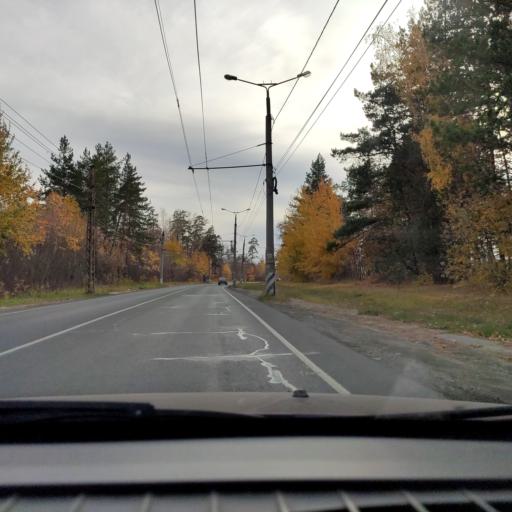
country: RU
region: Samara
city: Tol'yatti
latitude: 53.4908
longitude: 49.3851
